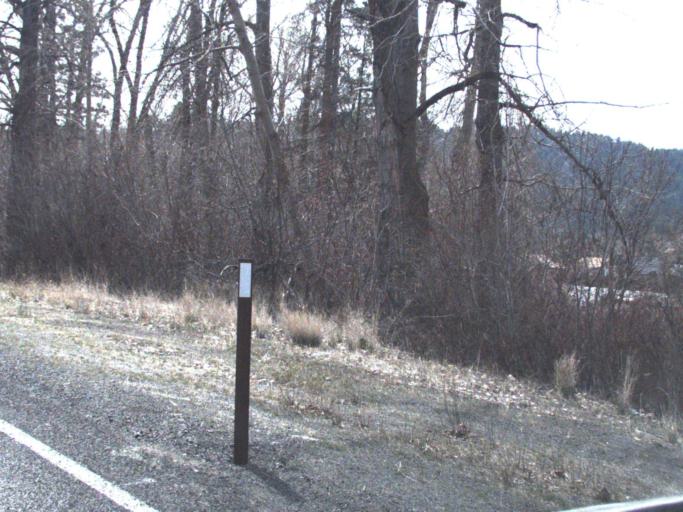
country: US
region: Washington
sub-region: Yakima County
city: Tieton
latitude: 46.8464
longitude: -120.9493
